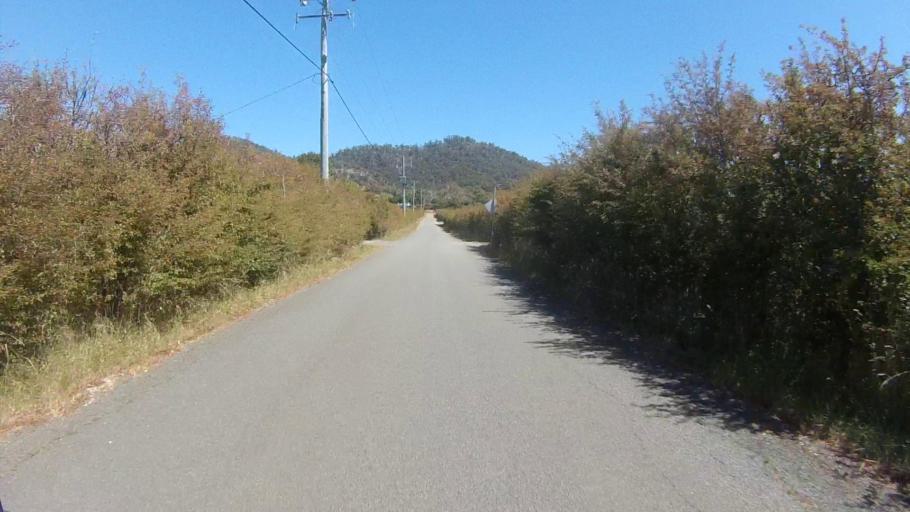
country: AU
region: Tasmania
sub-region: Clarence
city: Cambridge
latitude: -42.8445
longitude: 147.4588
